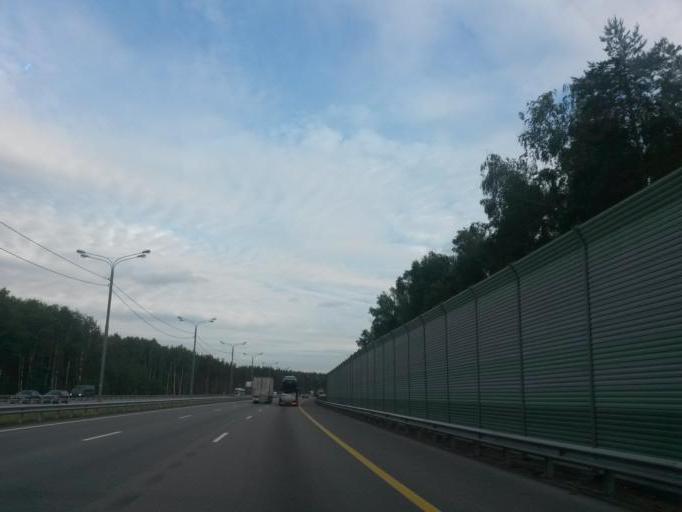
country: RU
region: Moskovskaya
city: Domodedovo
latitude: 55.4473
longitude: 37.7941
